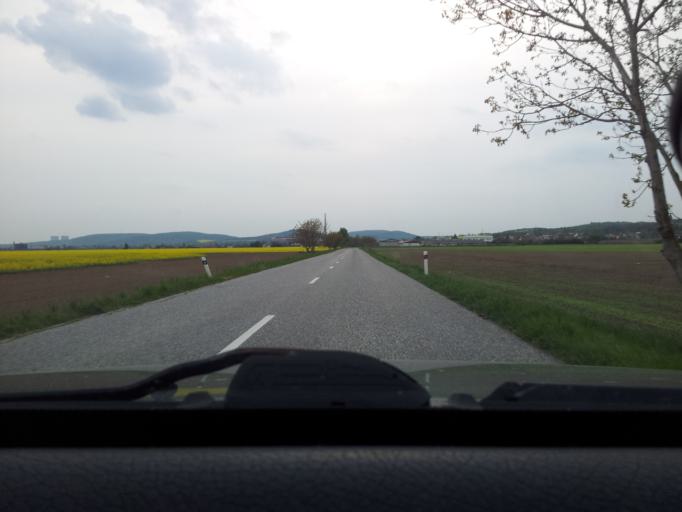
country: SK
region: Nitriansky
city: Tlmace
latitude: 48.2896
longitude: 18.5794
